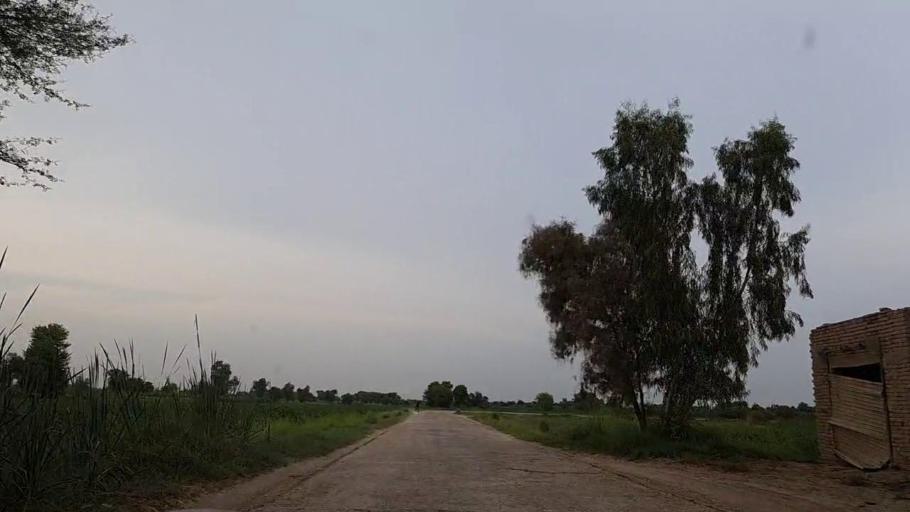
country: PK
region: Sindh
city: Mirpur Mathelo
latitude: 27.8872
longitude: 69.6396
